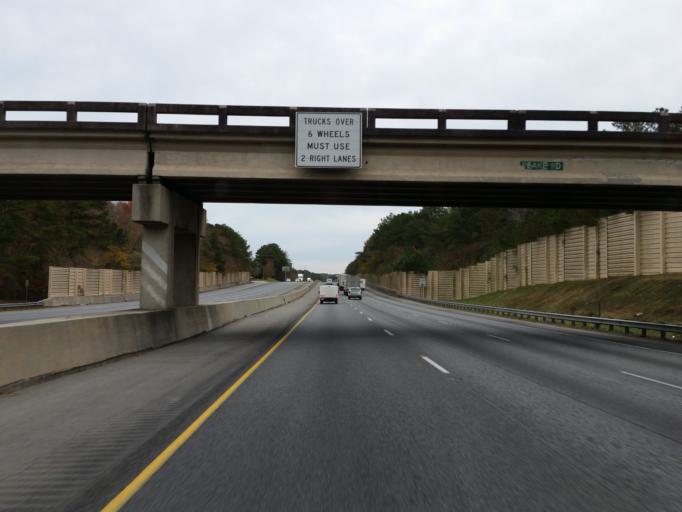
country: US
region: Georgia
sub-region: Bibb County
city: West Point
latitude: 32.8700
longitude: -83.7582
